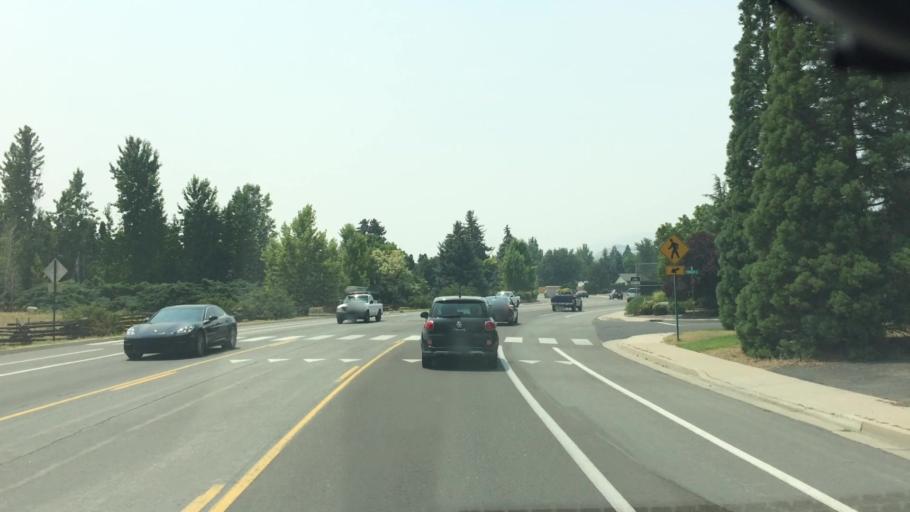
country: US
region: Nevada
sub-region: Washoe County
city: Reno
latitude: 39.4870
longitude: -119.8127
